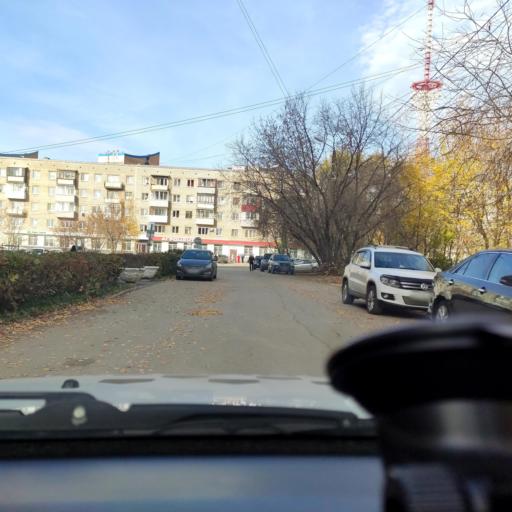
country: RU
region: Perm
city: Perm
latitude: 58.0203
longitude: 56.2713
